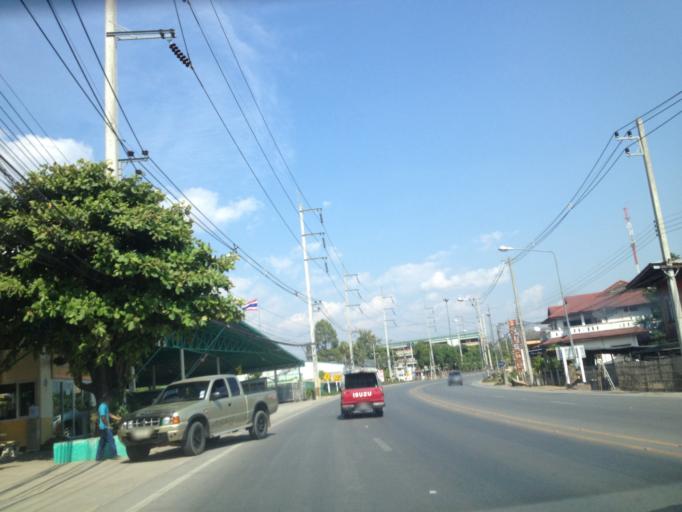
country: TH
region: Chiang Mai
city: Chom Thong
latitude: 18.4139
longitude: 98.6746
